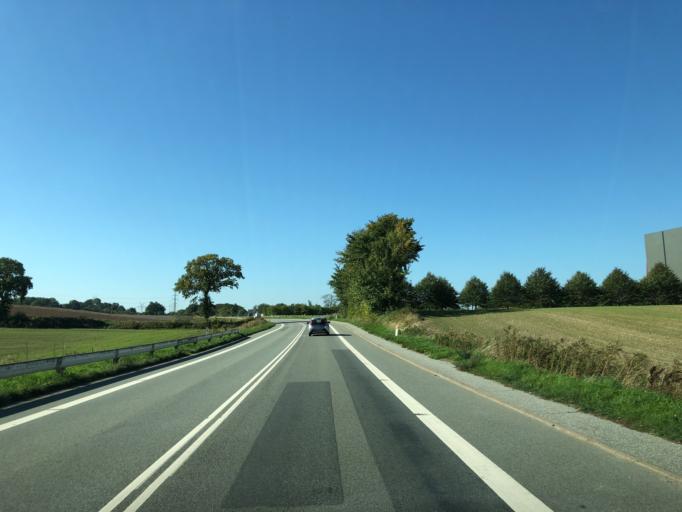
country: DK
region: South Denmark
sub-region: Aabenraa Kommune
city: Aabenraa
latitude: 55.0161
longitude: 9.4451
